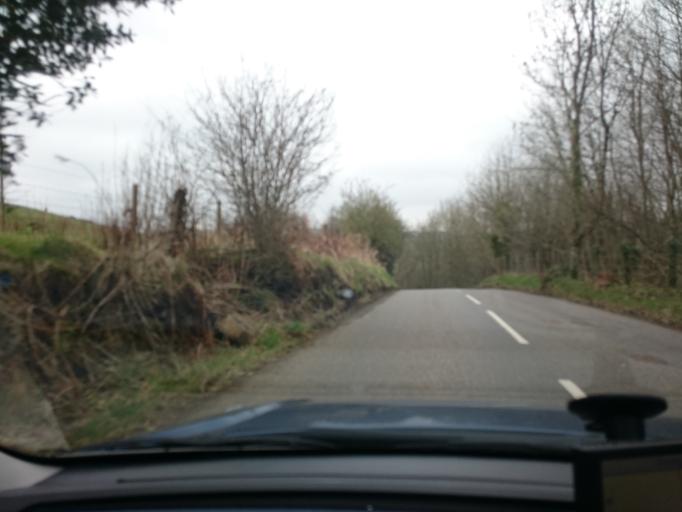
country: GB
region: Scotland
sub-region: Falkirk
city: Dunipace
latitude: 56.0257
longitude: -3.9459
